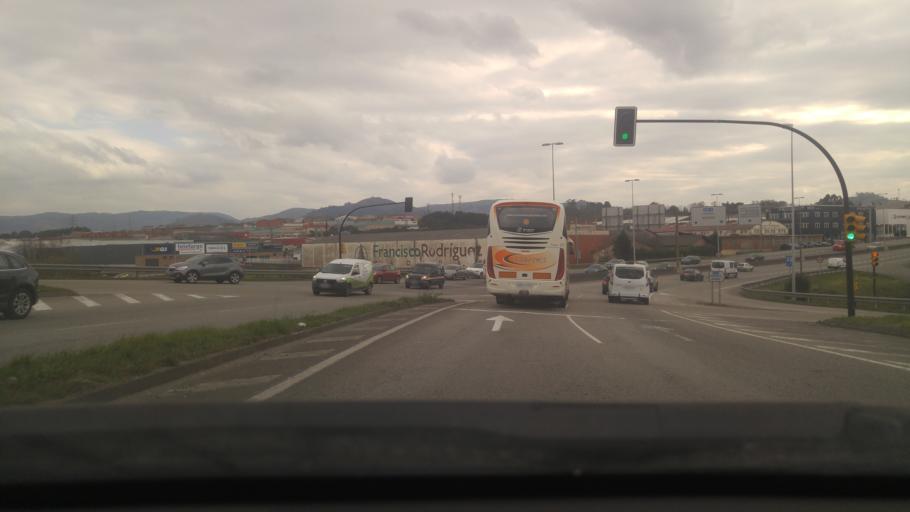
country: ES
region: Asturias
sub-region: Province of Asturias
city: Natahoyo
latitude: 43.5138
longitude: -5.6862
